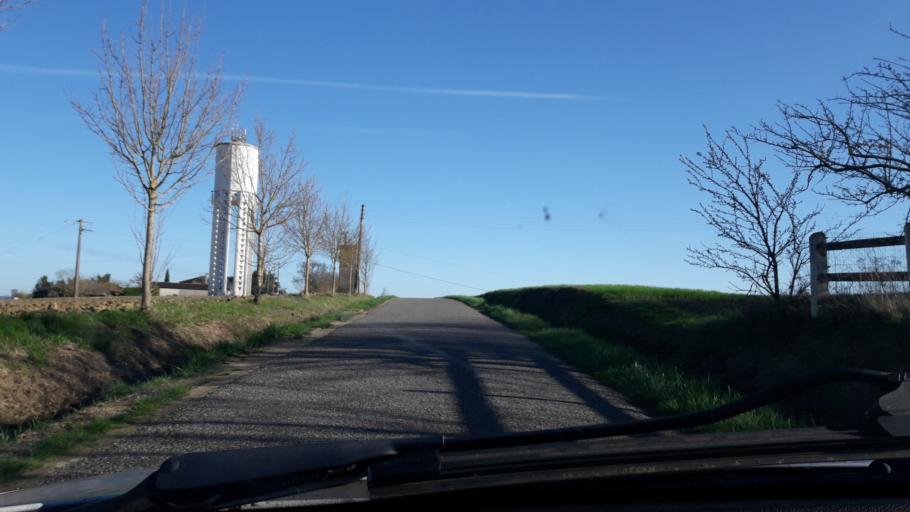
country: FR
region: Midi-Pyrenees
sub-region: Departement du Gers
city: Samatan
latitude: 43.5866
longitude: 0.9983
